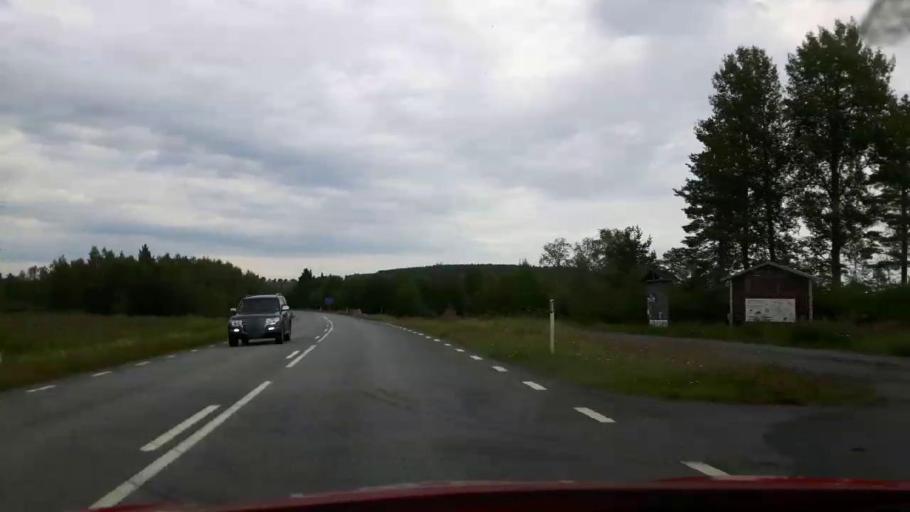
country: SE
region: Jaemtland
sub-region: Stroemsunds Kommun
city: Stroemsund
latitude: 63.5436
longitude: 15.3700
